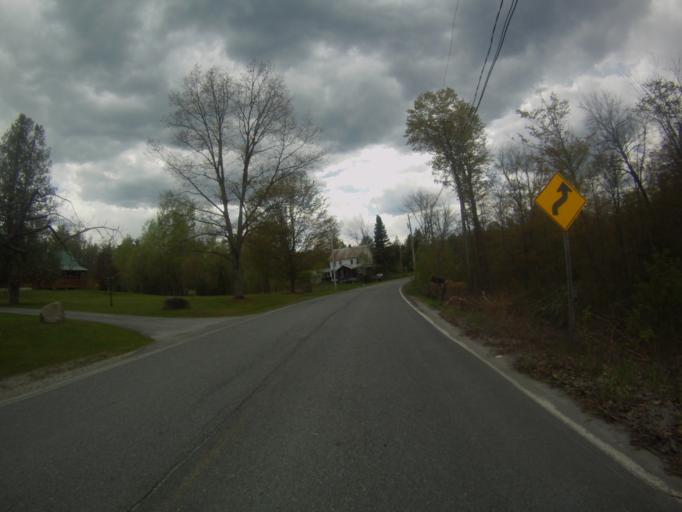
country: US
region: New York
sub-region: Essex County
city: Mineville
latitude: 44.0610
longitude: -73.5103
